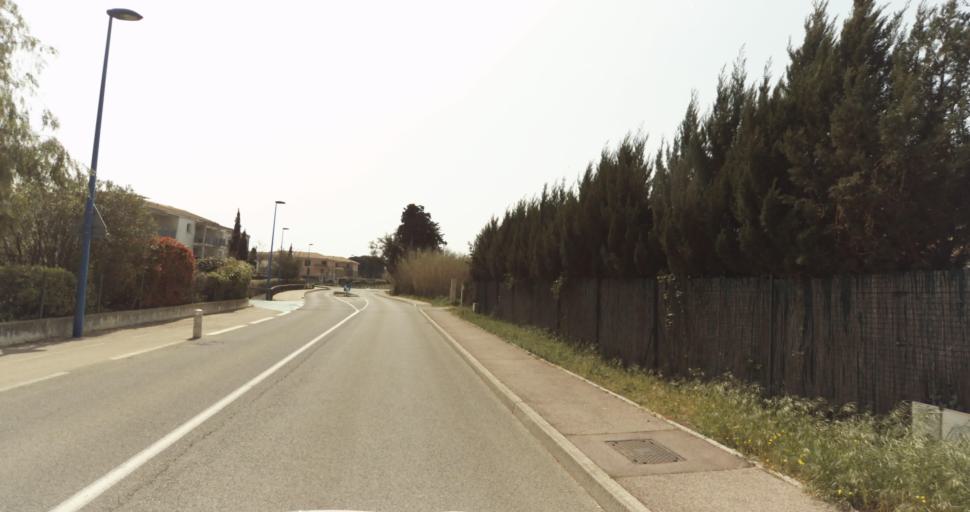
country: FR
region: Provence-Alpes-Cote d'Azur
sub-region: Departement du Var
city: Bormes-les-Mimosas
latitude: 43.1391
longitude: 6.3461
